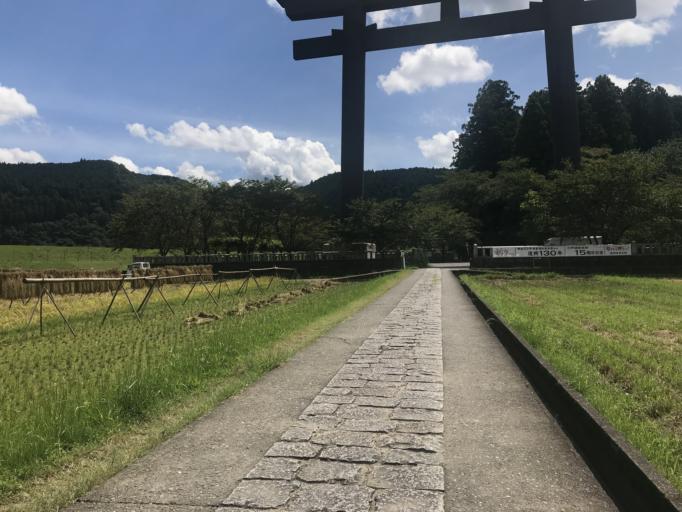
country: JP
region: Wakayama
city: Shingu
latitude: 33.8364
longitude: 135.7756
